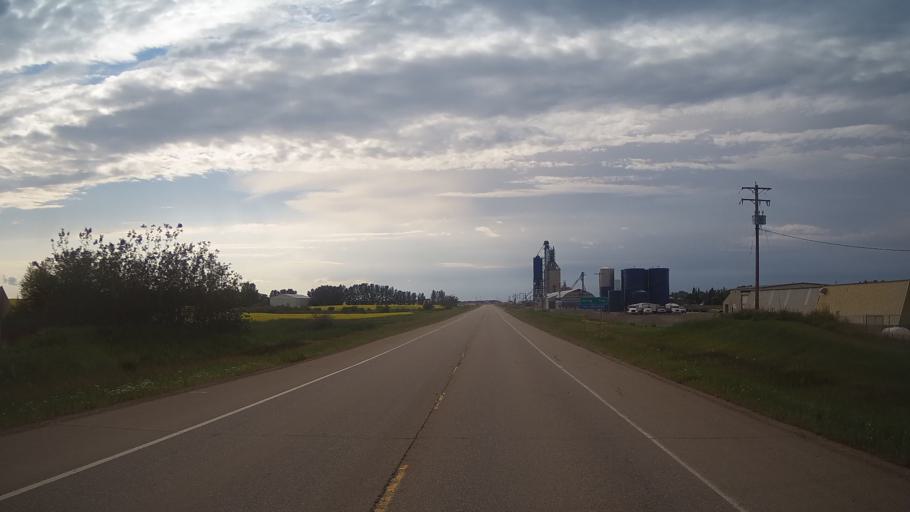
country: CA
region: Alberta
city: Viking
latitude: 53.0886
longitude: -111.7686
